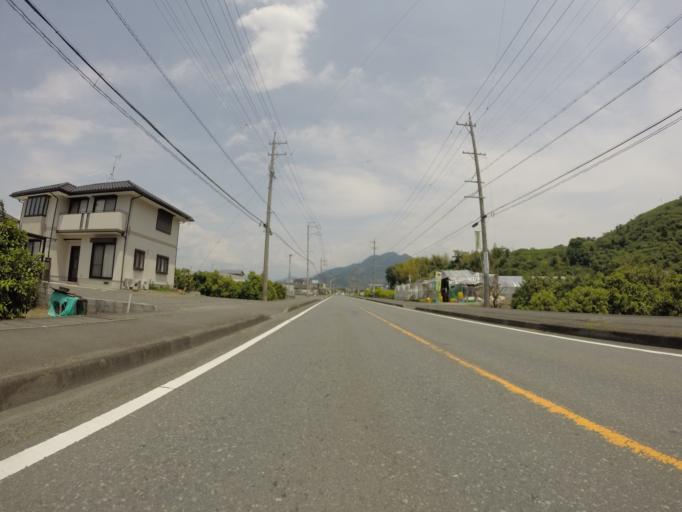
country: JP
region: Shizuoka
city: Shizuoka-shi
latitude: 35.0229
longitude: 138.3761
